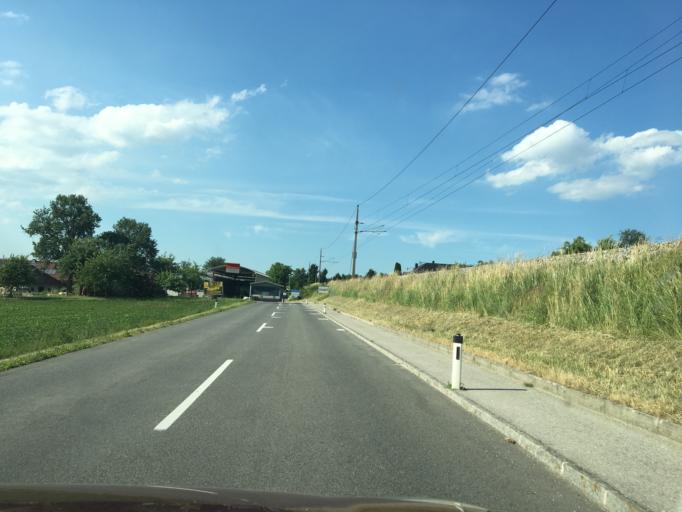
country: AT
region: Upper Austria
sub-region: Politischer Bezirk Urfahr-Umgebung
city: Engerwitzdorf
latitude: 48.2965
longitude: 14.4862
